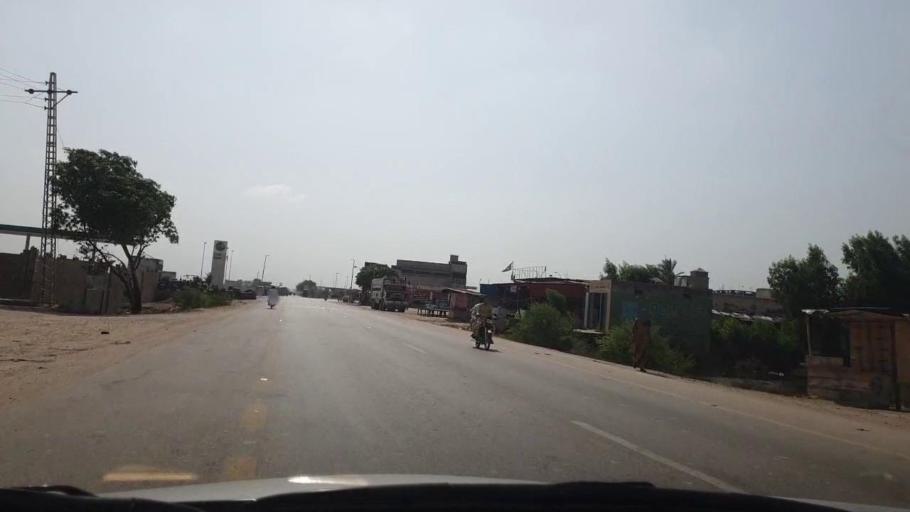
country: PK
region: Sindh
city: Matli
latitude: 25.0607
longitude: 68.6361
